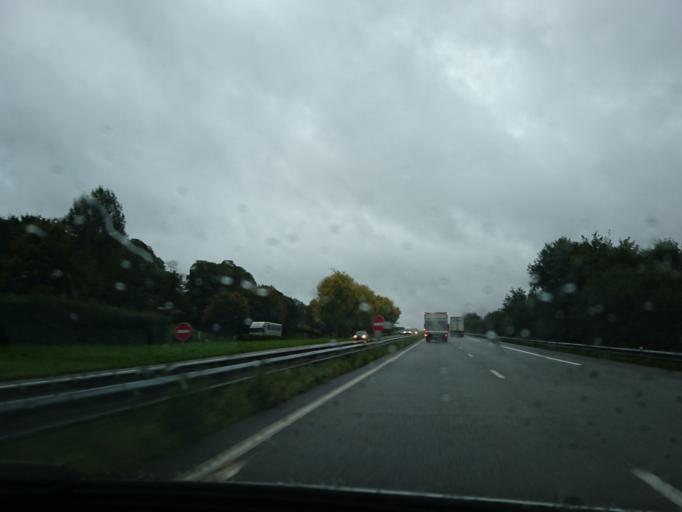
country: FR
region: Brittany
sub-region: Departement du Finistere
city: Chateaulin
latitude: 48.2401
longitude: -4.1062
